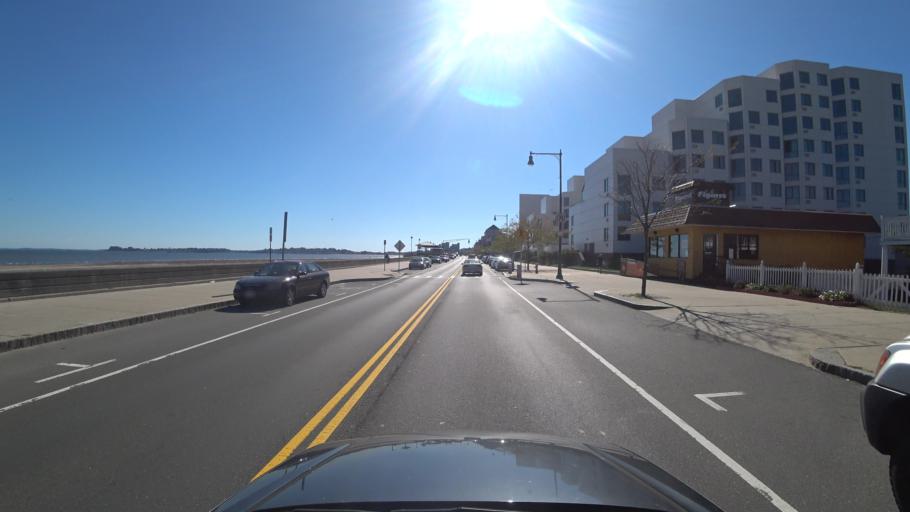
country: US
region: Massachusetts
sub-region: Suffolk County
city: Revere
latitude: 42.4249
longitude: -70.9827
